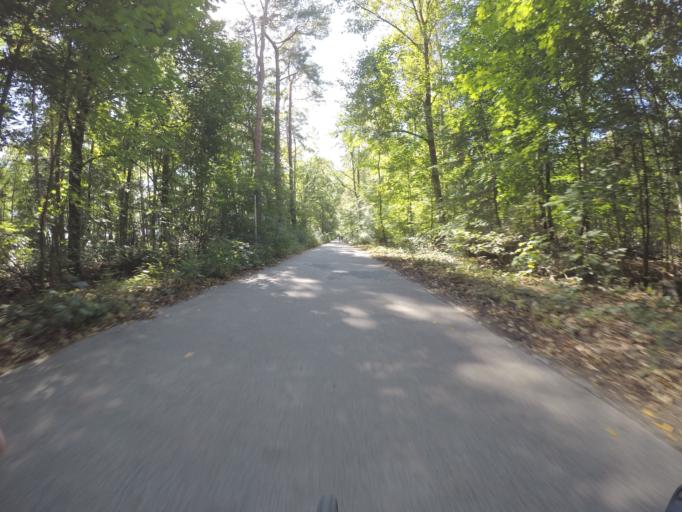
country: DE
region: Berlin
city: Konradshohe
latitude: 52.5879
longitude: 13.2549
